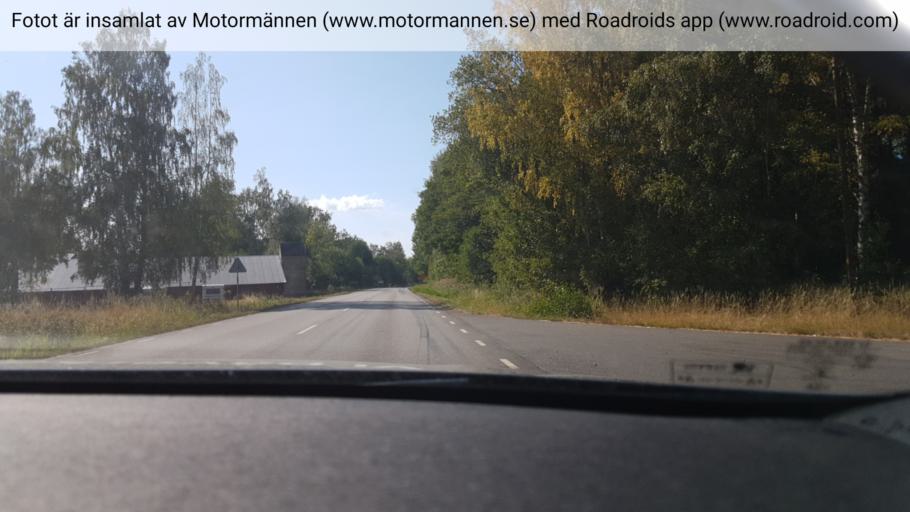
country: SE
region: Vaestra Goetaland
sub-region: Gotene Kommun
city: Goetene
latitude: 58.6271
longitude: 13.4570
